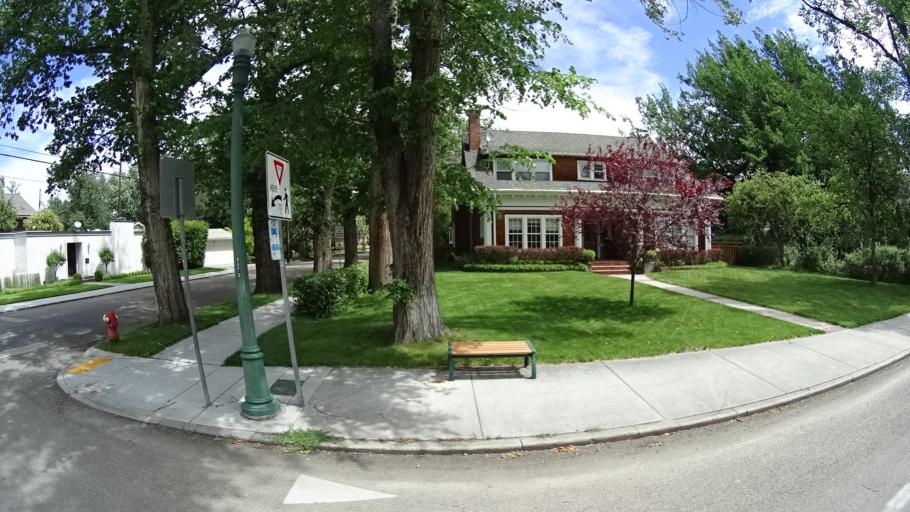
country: US
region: Idaho
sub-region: Ada County
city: Boise
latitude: 43.6070
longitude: -116.1823
